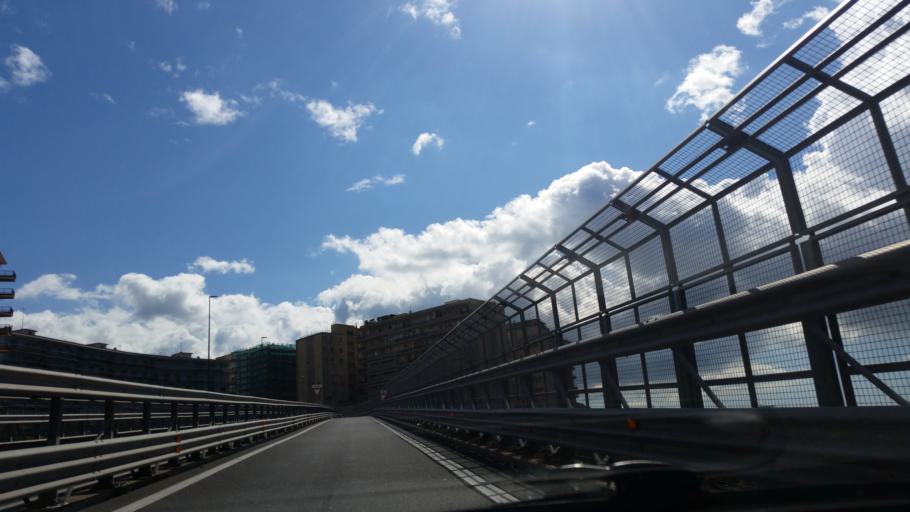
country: IT
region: Campania
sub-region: Provincia di Napoli
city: Napoli
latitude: 40.8440
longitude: 14.2188
